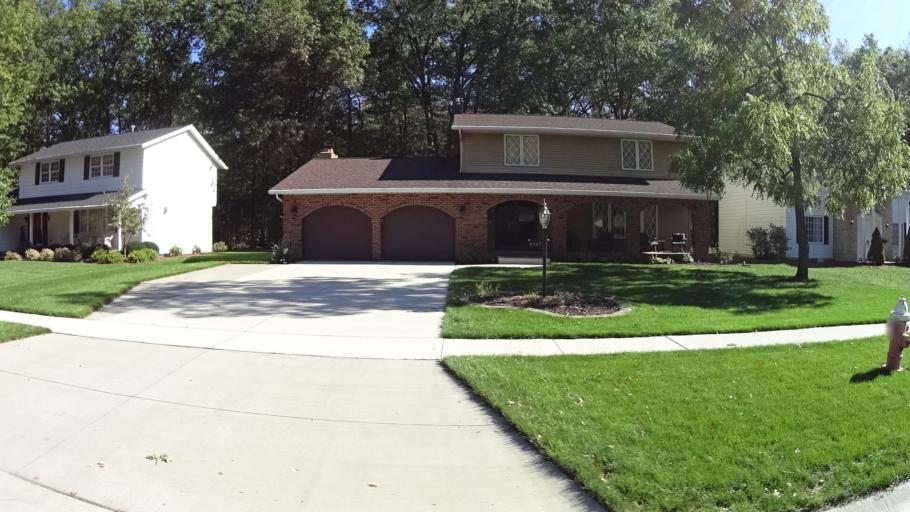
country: US
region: Ohio
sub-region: Lorain County
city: Lorain
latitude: 41.4308
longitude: -82.1797
